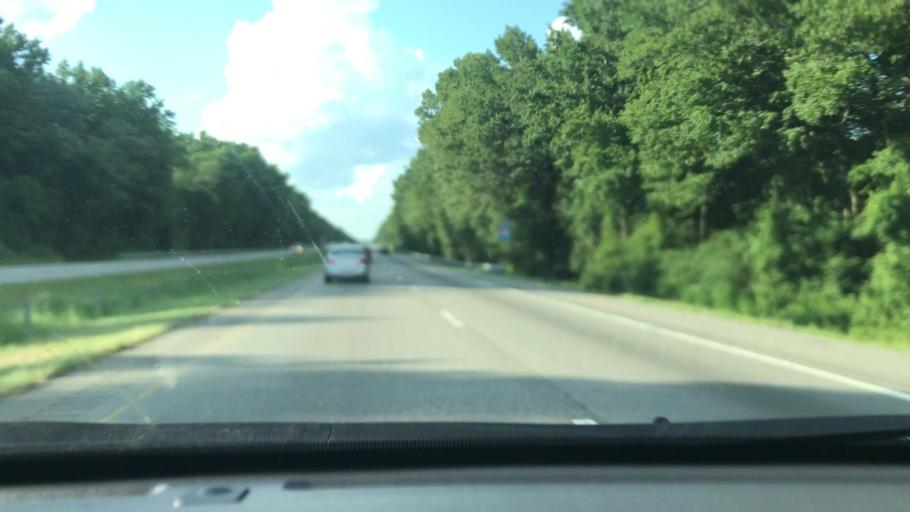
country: US
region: North Carolina
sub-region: Robeson County
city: Saint Pauls
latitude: 34.7268
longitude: -78.9972
